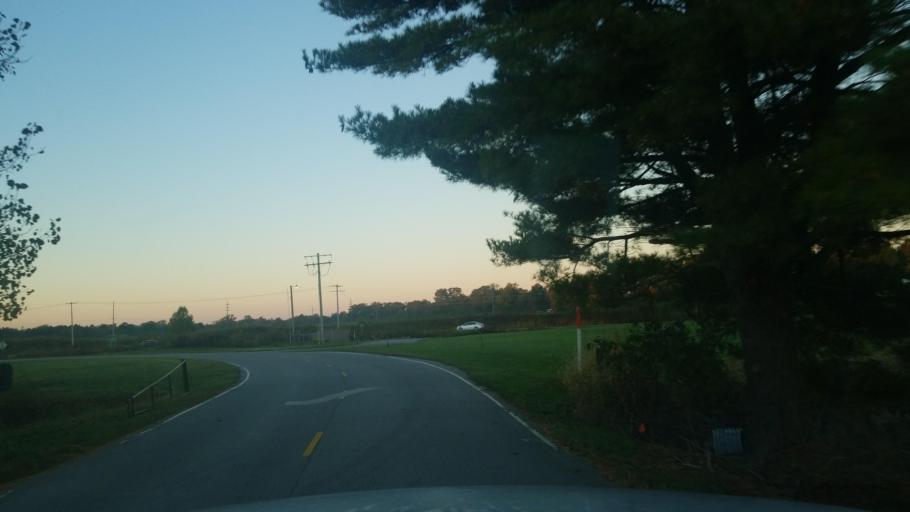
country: US
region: Illinois
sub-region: Williamson County
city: Energy
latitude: 37.7437
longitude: -89.0205
